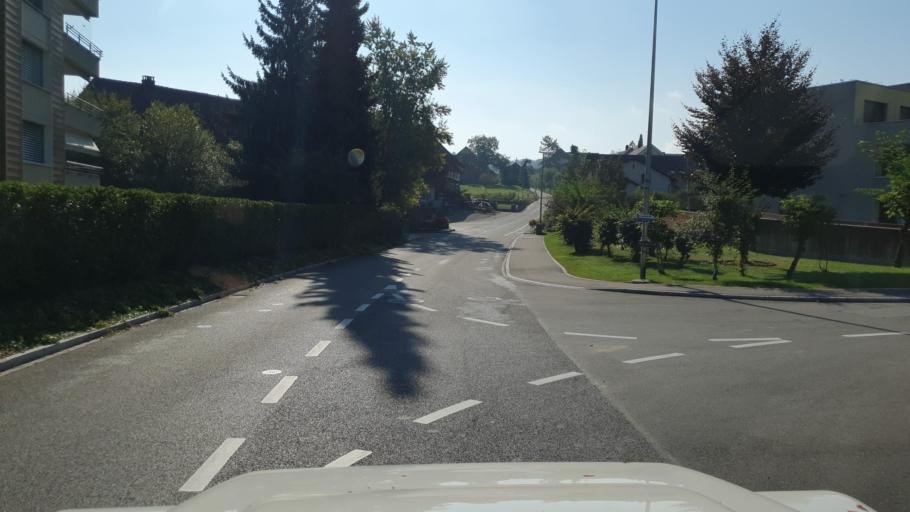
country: CH
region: Aargau
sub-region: Bezirk Bremgarten
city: Villmergen
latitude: 47.3430
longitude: 8.2458
